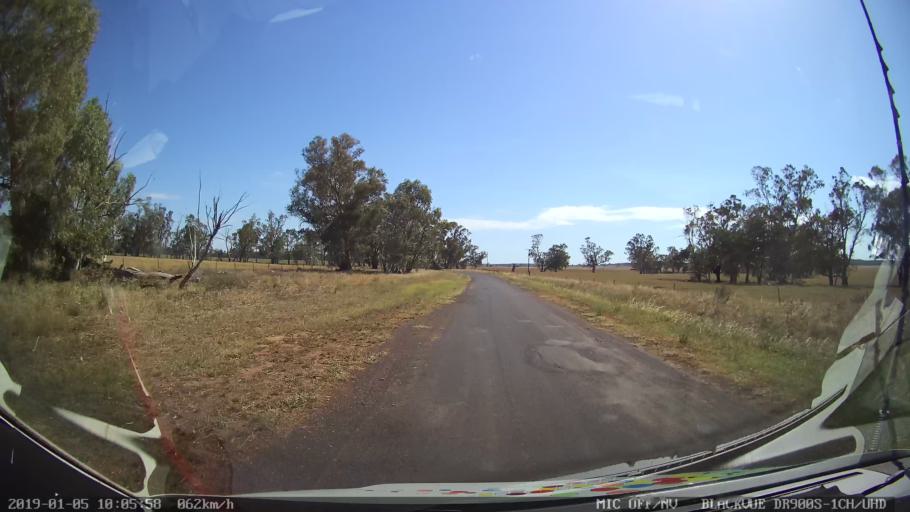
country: AU
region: New South Wales
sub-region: Gilgandra
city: Gilgandra
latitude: -31.6615
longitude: 148.8681
